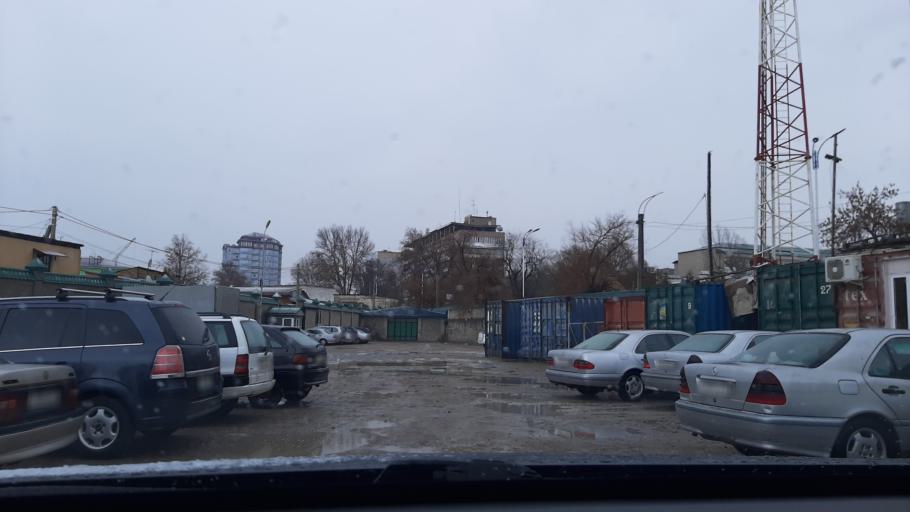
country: TJ
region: Viloyati Sughd
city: Khujand
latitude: 40.2785
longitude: 69.6368
